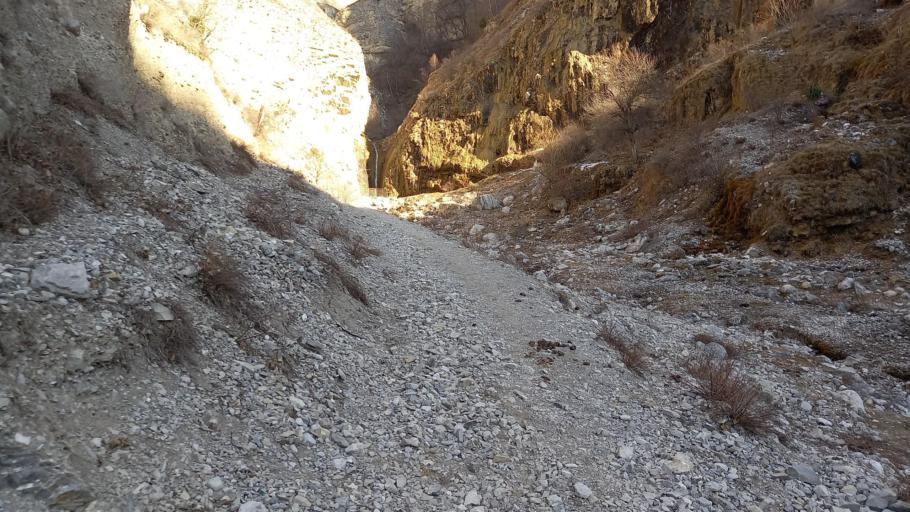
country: RU
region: Ingushetiya
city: Dzhayrakh
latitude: 42.8456
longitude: 44.6652
